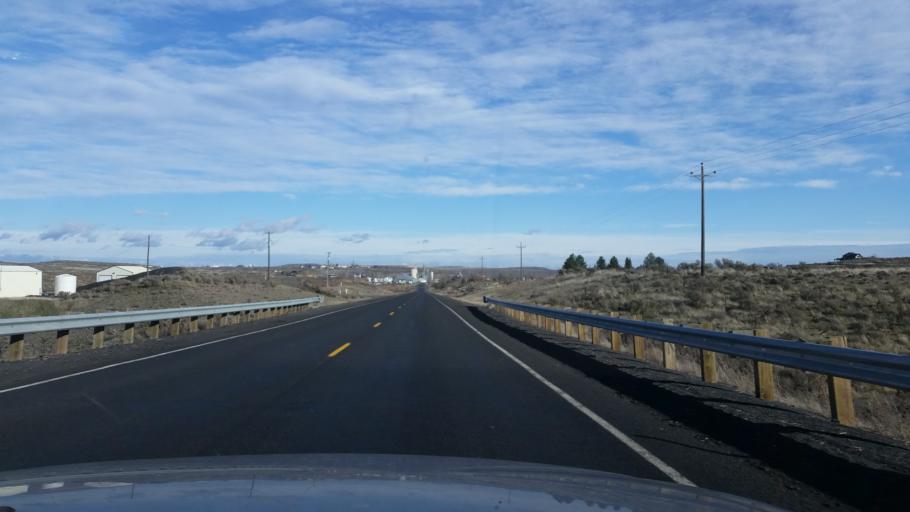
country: US
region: Washington
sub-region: Adams County
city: Ritzville
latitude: 47.3273
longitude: -118.7151
